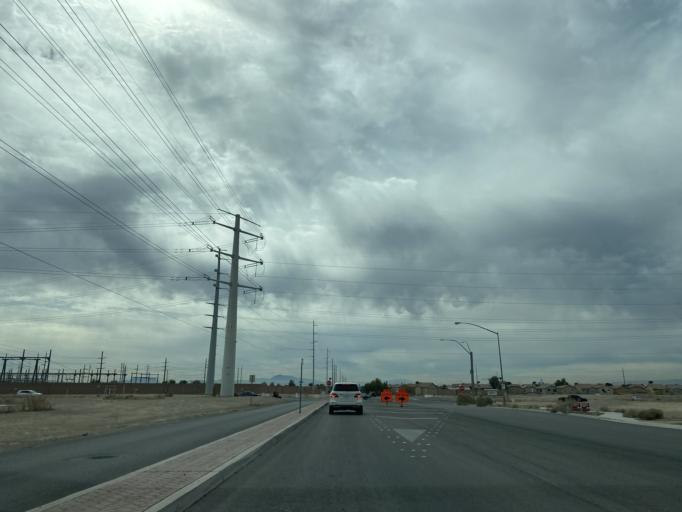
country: US
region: Nevada
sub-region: Clark County
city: Nellis Air Force Base
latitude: 36.2777
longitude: -115.0987
